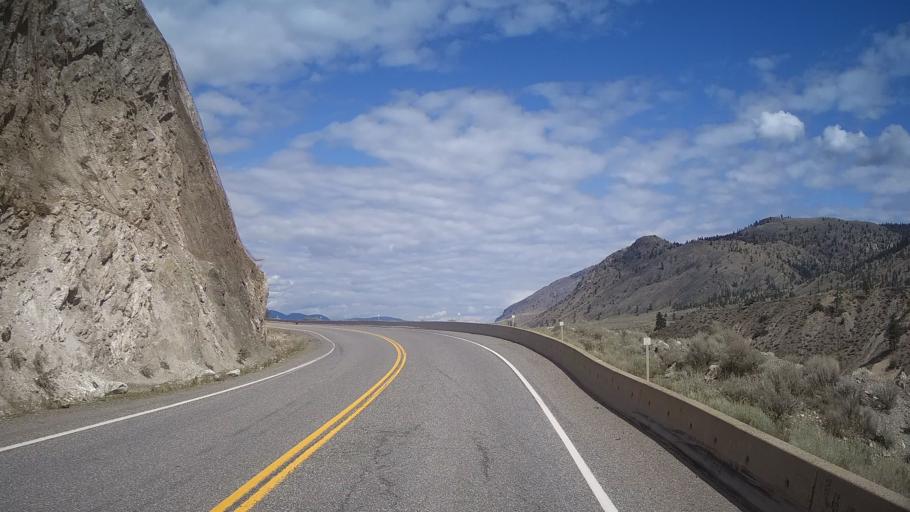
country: CA
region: British Columbia
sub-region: Thompson-Nicola Regional District
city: Ashcroft
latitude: 50.5374
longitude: -121.2867
